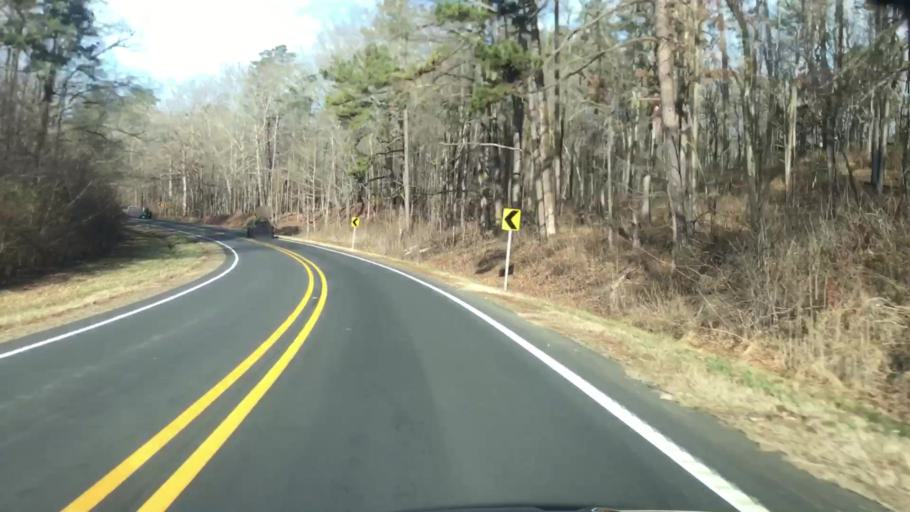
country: US
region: Arkansas
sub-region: Montgomery County
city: Mount Ida
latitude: 34.5231
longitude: -93.3920
